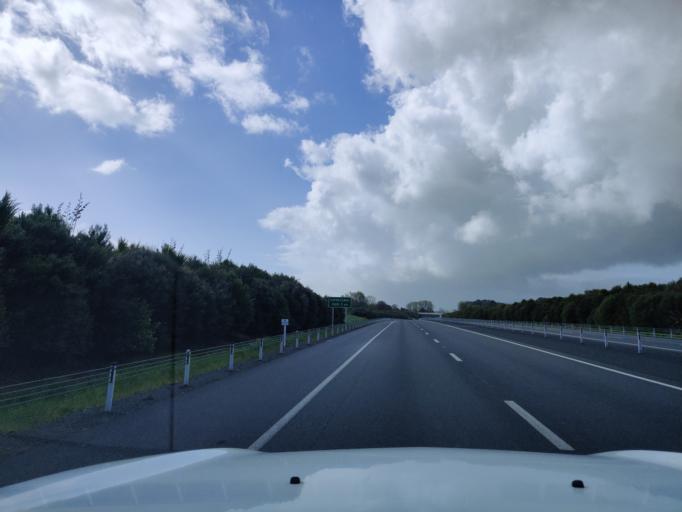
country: NZ
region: Waikato
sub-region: Waipa District
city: Cambridge
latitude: -37.8798
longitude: 175.4877
